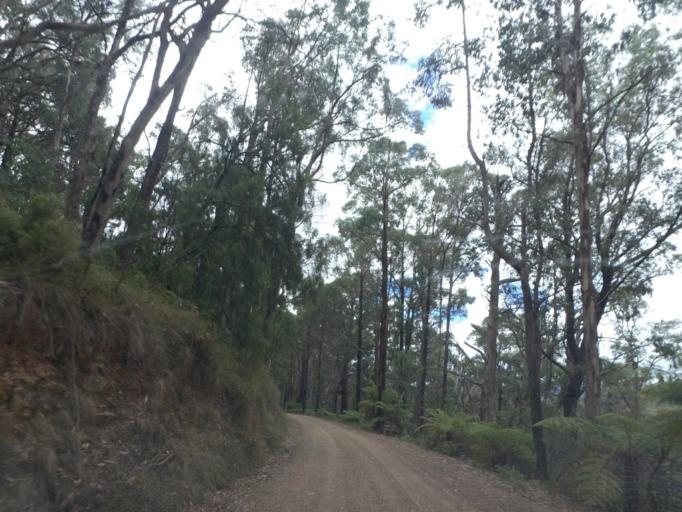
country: AU
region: Victoria
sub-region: Murrindindi
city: Alexandra
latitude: -37.4431
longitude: 145.9667
